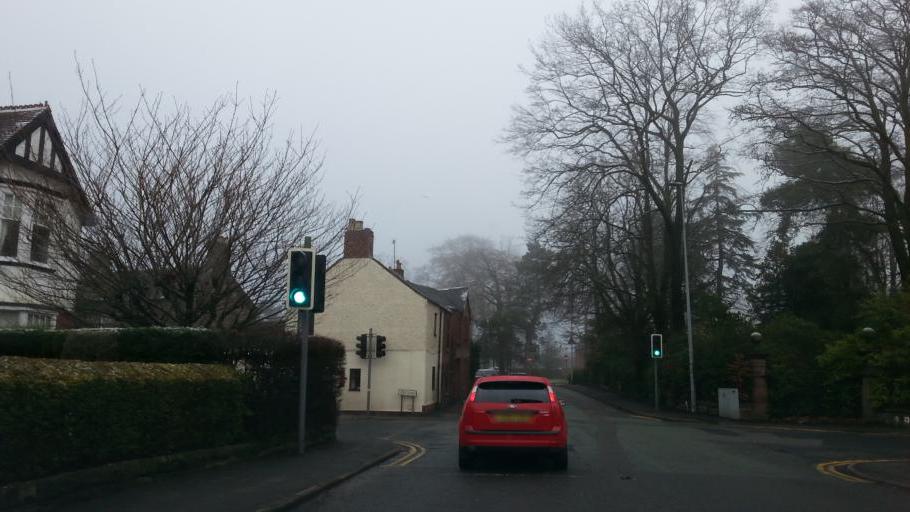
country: GB
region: England
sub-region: Cheshire East
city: Congleton
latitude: 53.1534
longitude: -2.1843
